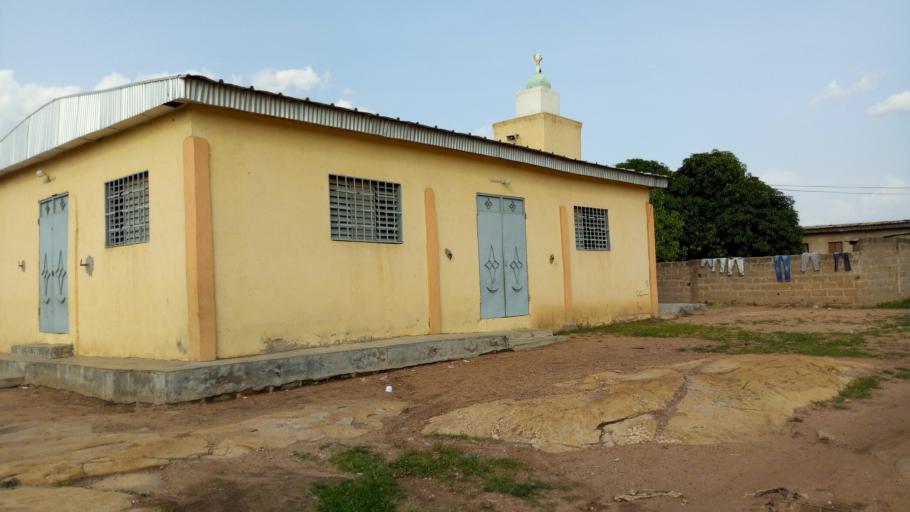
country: CI
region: Vallee du Bandama
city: Bouake
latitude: 7.7335
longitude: -5.0428
